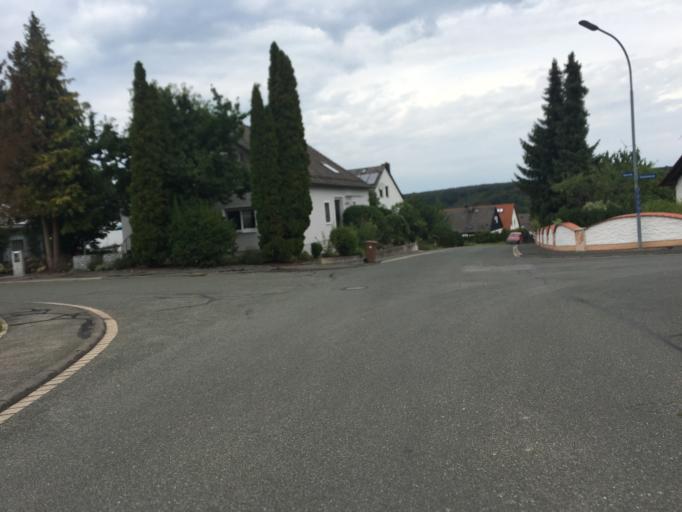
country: DE
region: Bavaria
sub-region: Regierungsbezirk Mittelfranken
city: Wilhermsdorf
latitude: 49.4810
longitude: 10.7057
